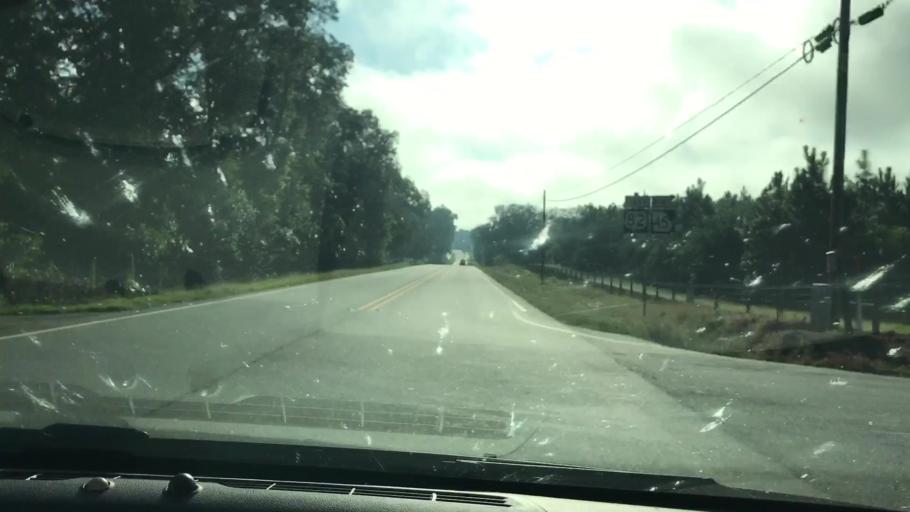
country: US
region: Georgia
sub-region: Terrell County
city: Dawson
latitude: 31.7695
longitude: -84.4710
